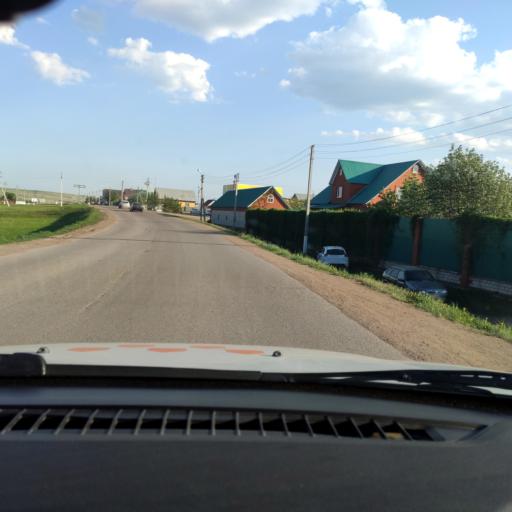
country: RU
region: Bashkortostan
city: Karmaskaly
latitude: 54.3637
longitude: 56.1580
